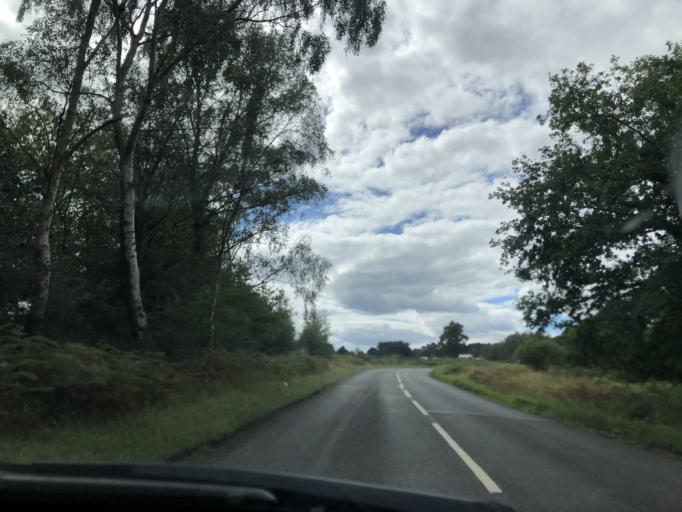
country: GB
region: England
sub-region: East Sussex
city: Forest Row
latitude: 51.0751
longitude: 0.0578
